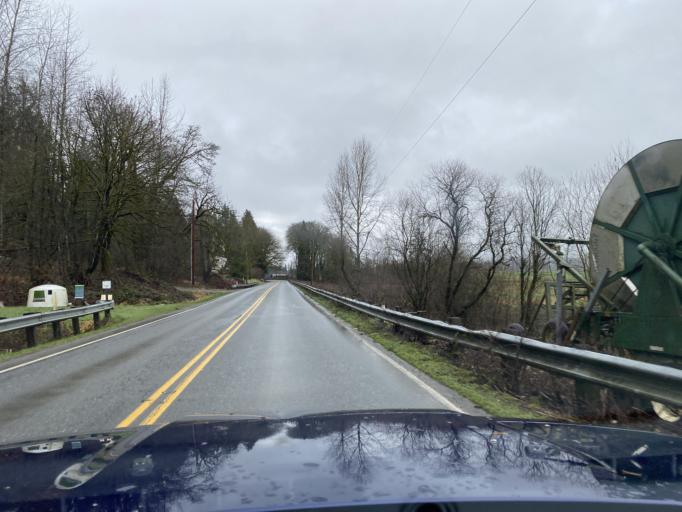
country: US
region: Washington
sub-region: King County
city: Duvall
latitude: 47.7627
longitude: -122.0020
